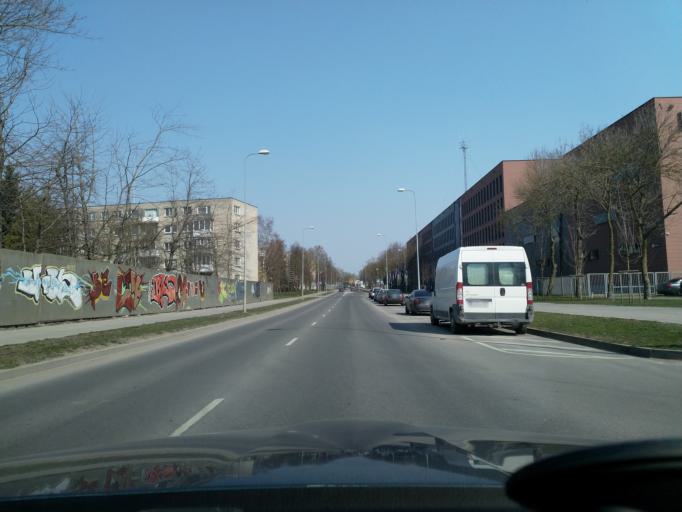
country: LT
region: Klaipedos apskritis
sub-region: Klaipeda
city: Klaipeda
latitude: 55.6970
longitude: 21.1599
